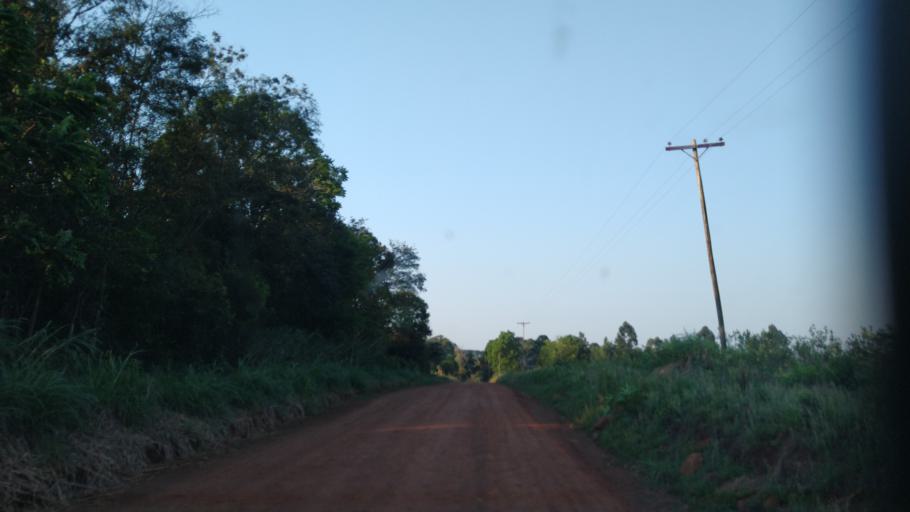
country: AR
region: Misiones
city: Jardin America
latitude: -27.0808
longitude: -55.2735
